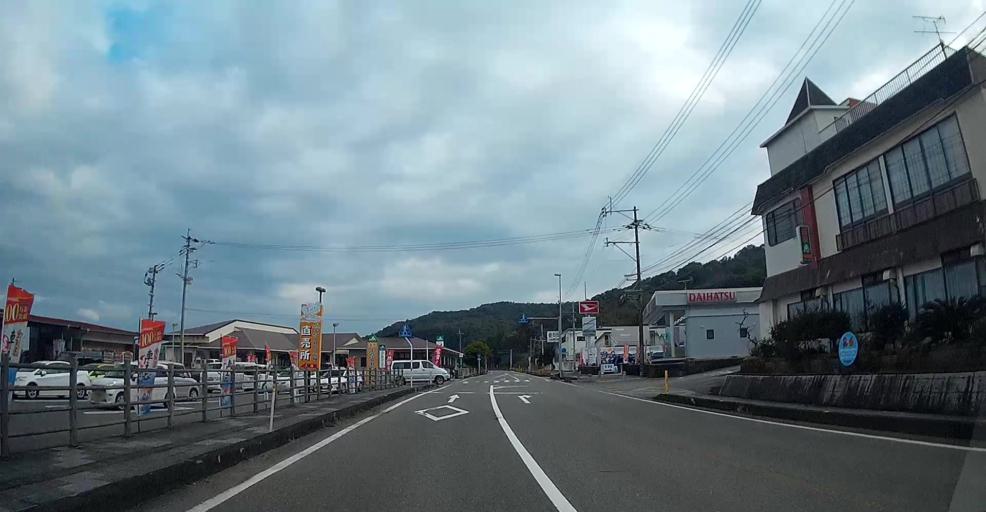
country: JP
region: Kumamoto
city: Hondo
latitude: 32.4523
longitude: 130.2089
